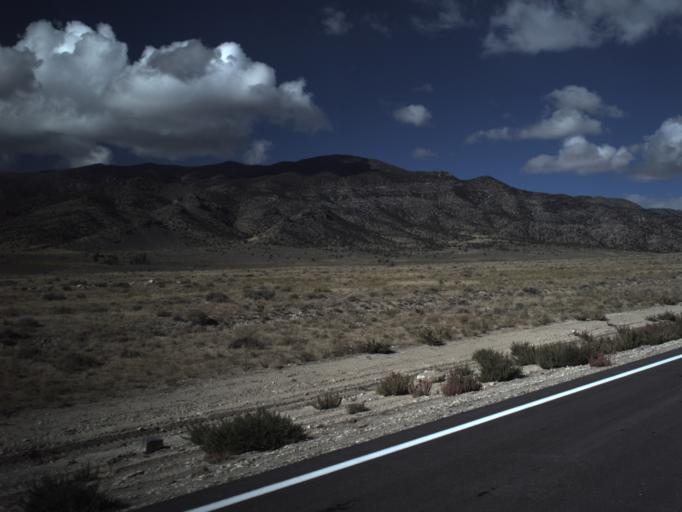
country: US
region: Utah
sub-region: Beaver County
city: Milford
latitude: 38.4947
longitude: -113.4815
